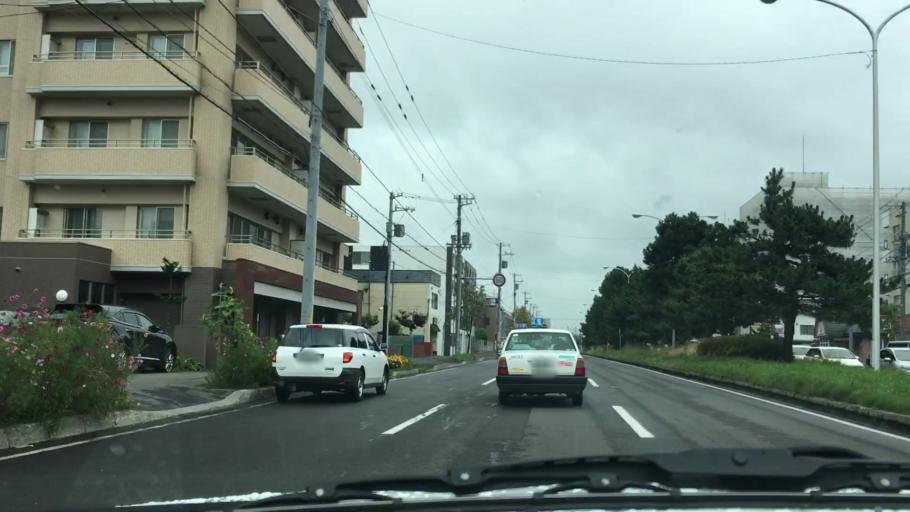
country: JP
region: Hokkaido
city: Sapporo
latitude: 43.0806
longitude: 141.3642
